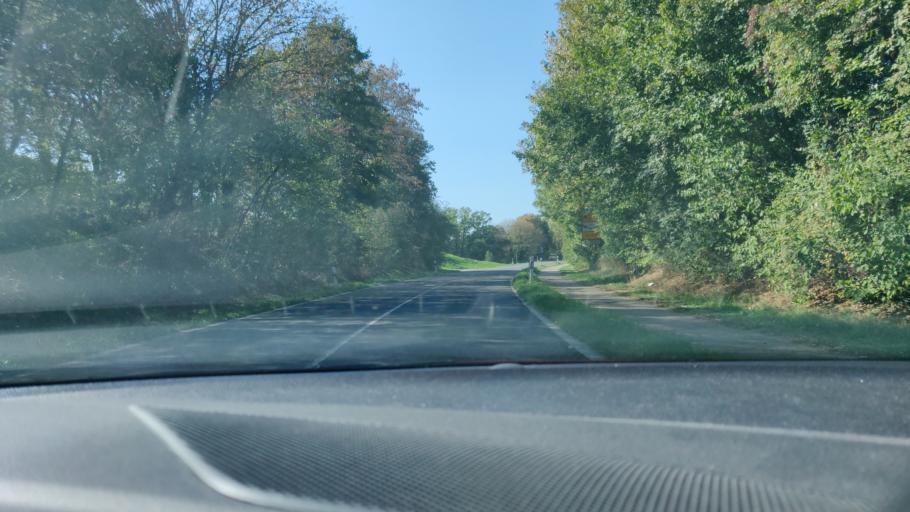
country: DE
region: North Rhine-Westphalia
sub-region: Regierungsbezirk Dusseldorf
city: Velbert
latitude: 51.3516
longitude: 7.0910
